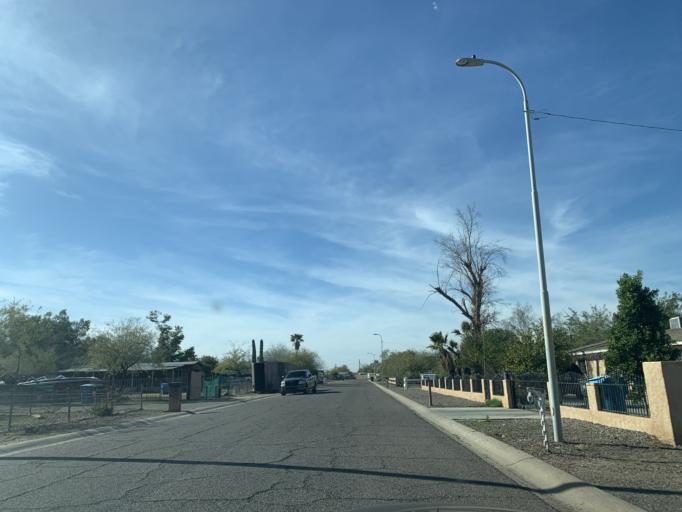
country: US
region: Arizona
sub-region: Maricopa County
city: Laveen
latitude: 33.3950
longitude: -112.1384
